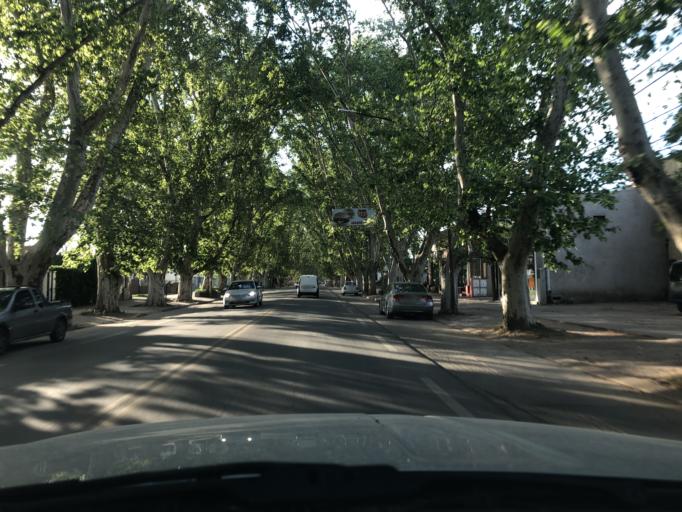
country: AR
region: Cordoba
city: Jesus Maria
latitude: -31.0162
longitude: -64.0677
